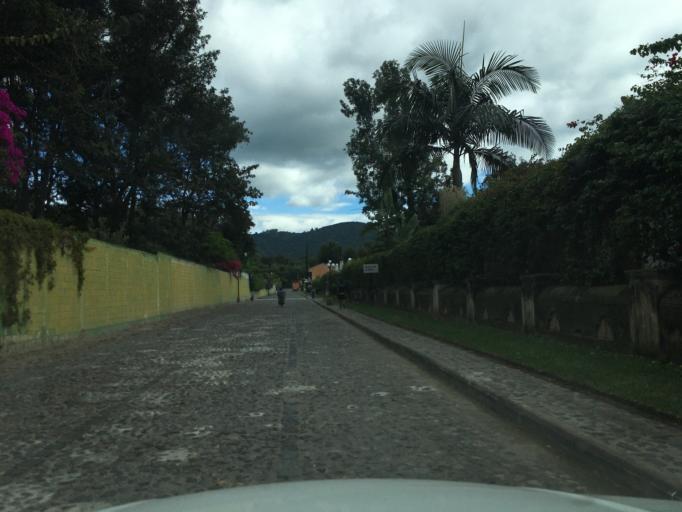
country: GT
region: Sacatepequez
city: Antigua Guatemala
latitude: 14.5497
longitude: -90.7372
